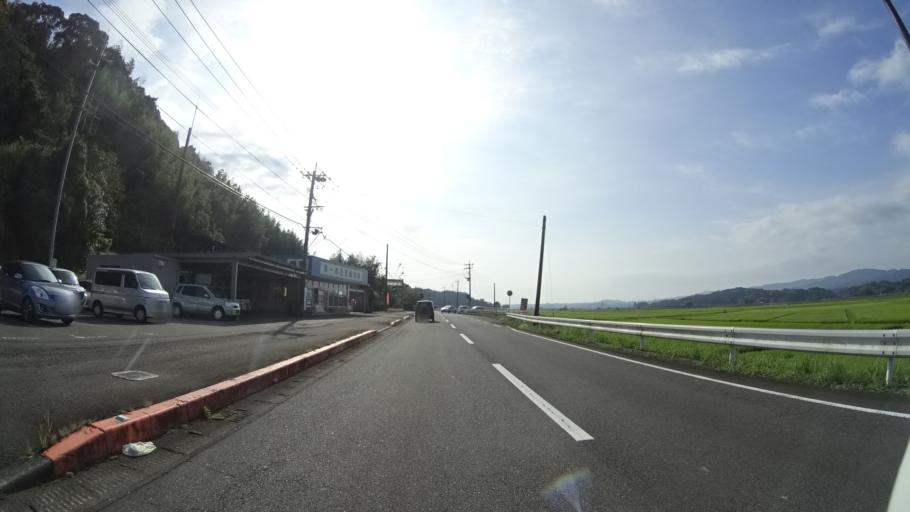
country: JP
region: Kagoshima
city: Okuchi-shinohara
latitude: 32.0204
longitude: 130.6150
